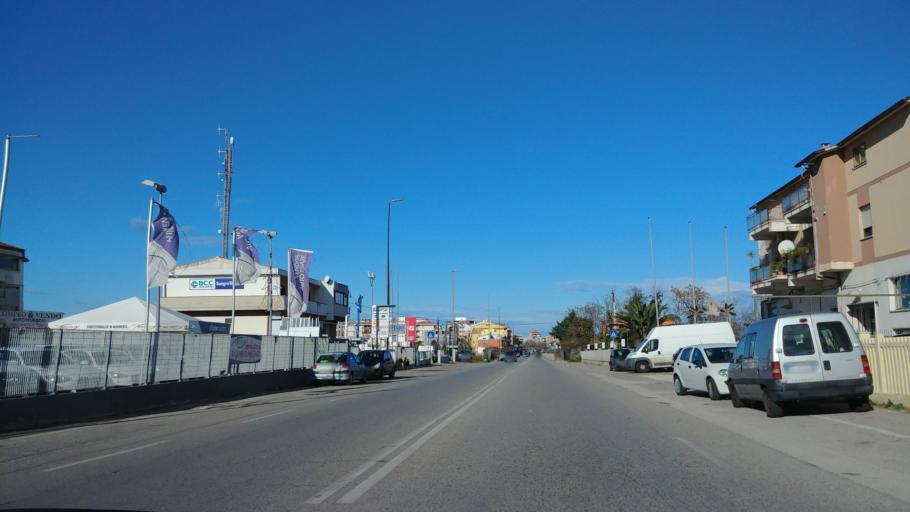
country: IT
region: Molise
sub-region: Provincia di Campobasso
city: Termoli
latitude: 41.9886
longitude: 15.0017
